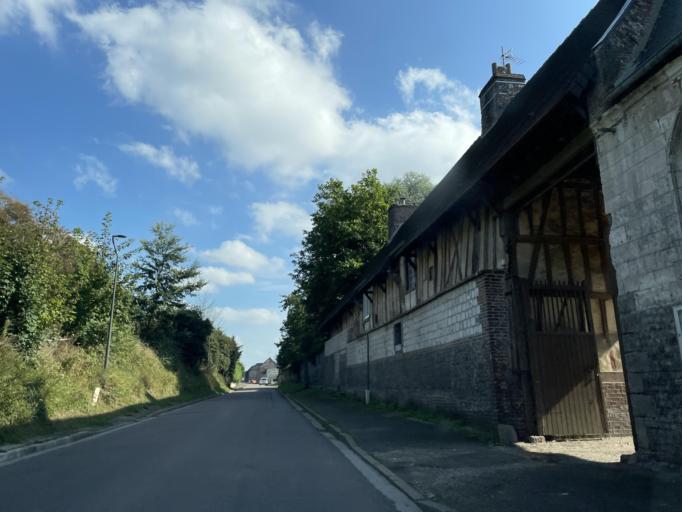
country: FR
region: Haute-Normandie
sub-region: Departement de la Seine-Maritime
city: Criel-sur-Mer
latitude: 50.0396
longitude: 1.3391
